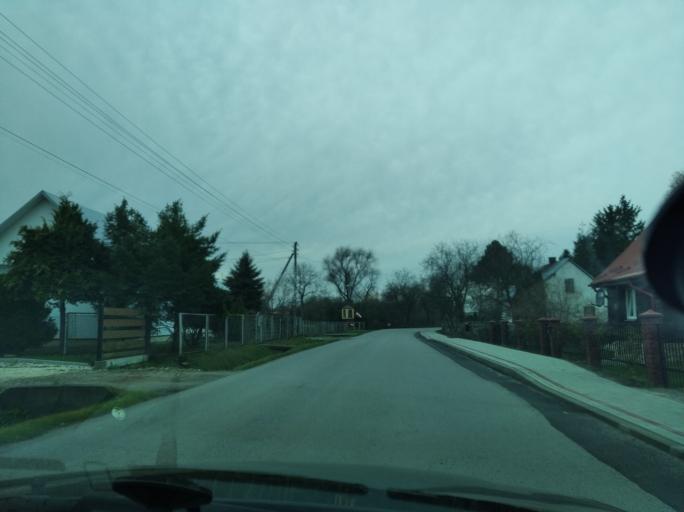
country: PL
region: Subcarpathian Voivodeship
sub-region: Powiat przeworski
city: Grzeska
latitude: 50.0844
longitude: 22.4483
